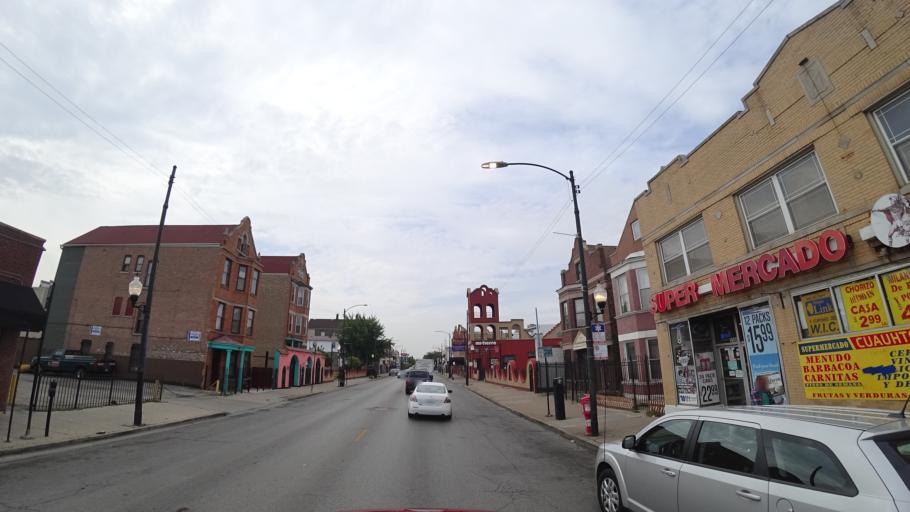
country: US
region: Illinois
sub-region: Cook County
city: Cicero
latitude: 41.8462
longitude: -87.7051
